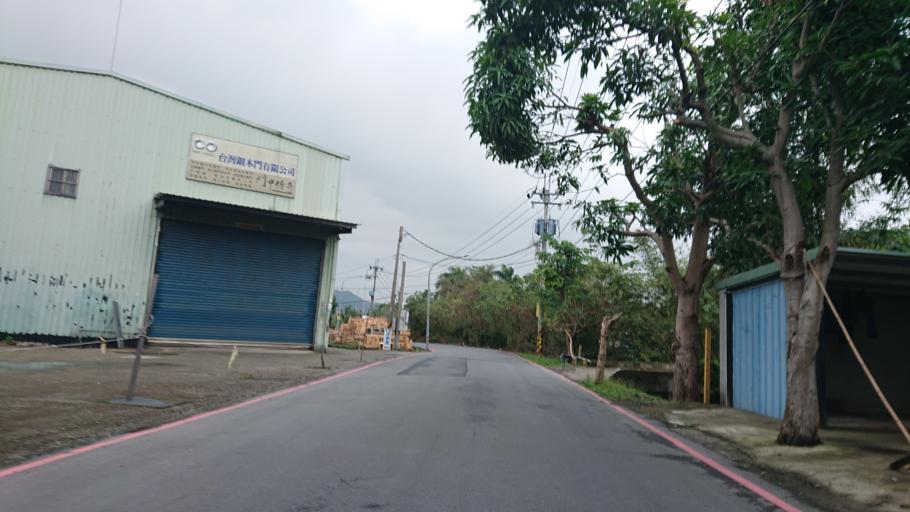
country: TW
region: Taiwan
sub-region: Taoyuan
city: Taoyuan
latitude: 24.9499
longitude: 121.3898
